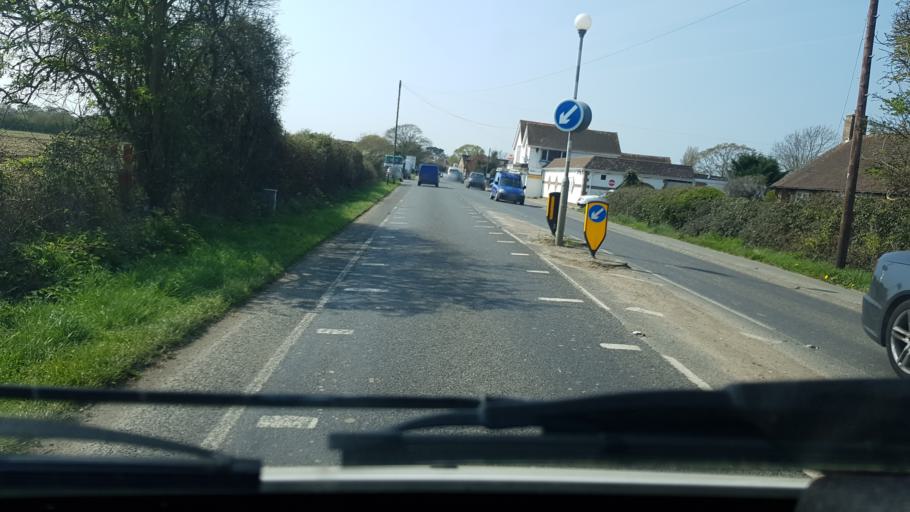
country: GB
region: England
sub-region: West Sussex
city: Birdham
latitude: 50.7907
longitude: -0.8356
